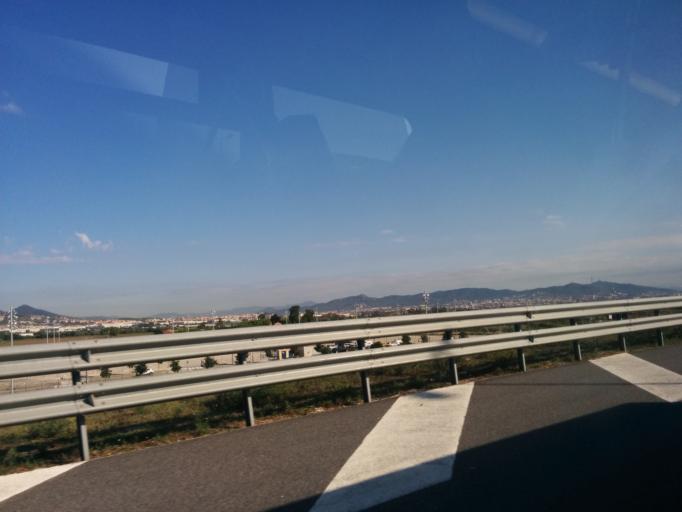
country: ES
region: Catalonia
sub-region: Provincia de Barcelona
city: Viladecans
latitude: 41.3010
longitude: 2.0535
